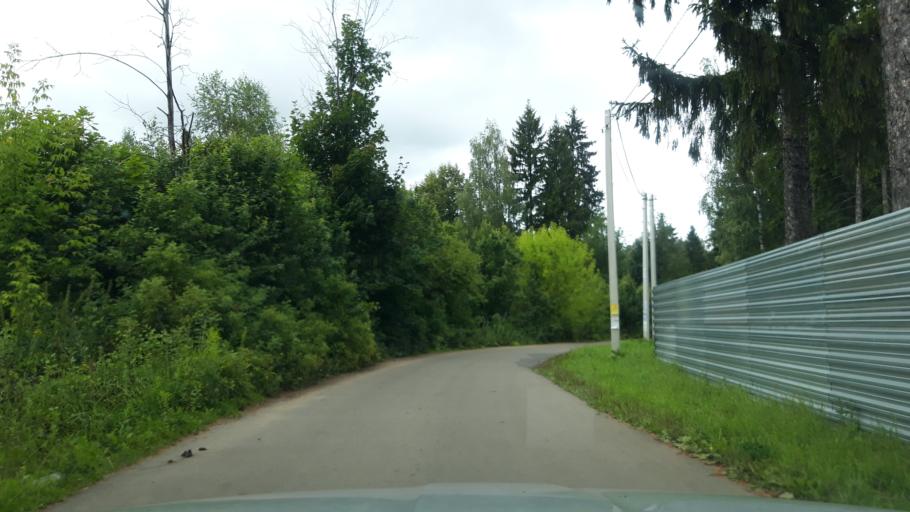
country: RU
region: Moskovskaya
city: Povarovo
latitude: 56.0615
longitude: 37.0703
